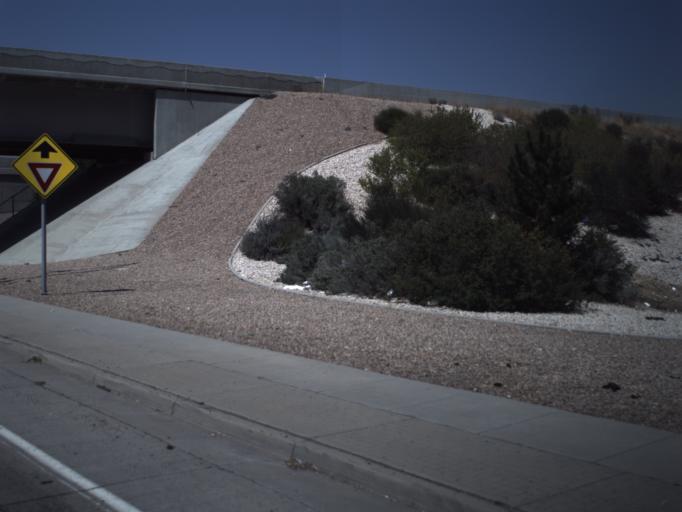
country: US
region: Utah
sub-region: Salt Lake County
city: Midvale
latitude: 40.6209
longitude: -111.9026
